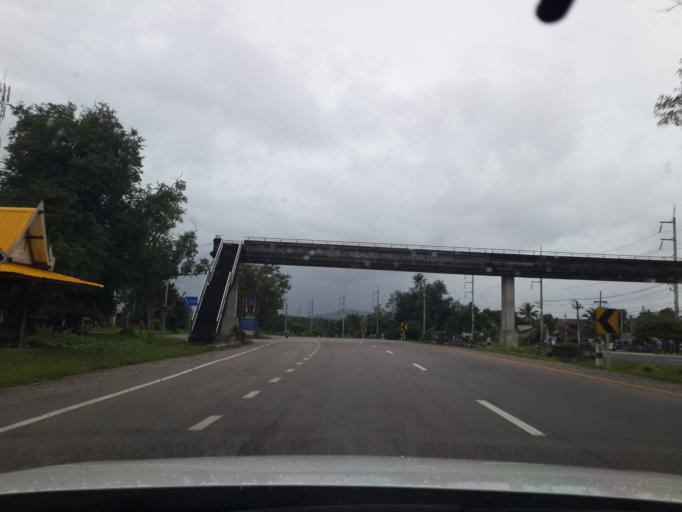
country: TH
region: Songkhla
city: Na Mom
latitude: 6.9705
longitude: 100.5755
